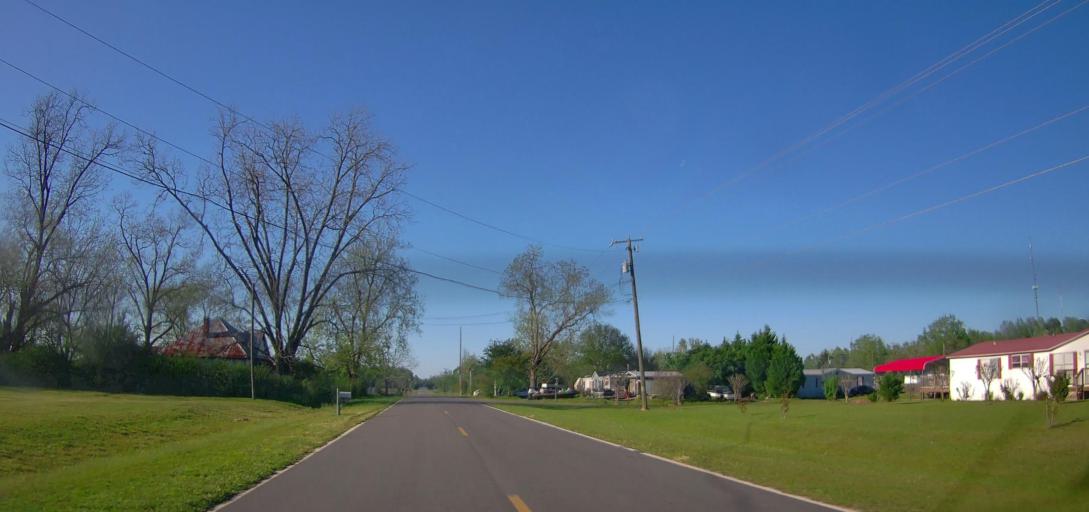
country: US
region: Georgia
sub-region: Ben Hill County
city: Fitzgerald
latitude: 31.7321
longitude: -83.2802
